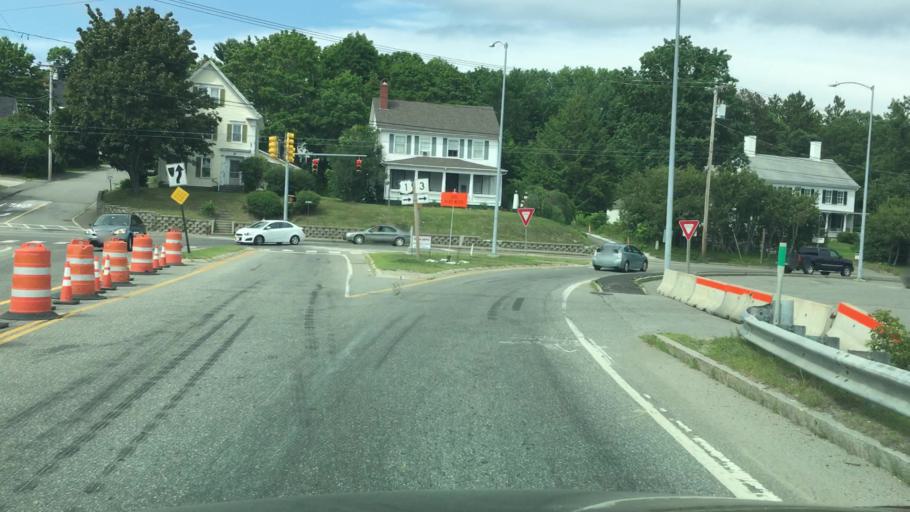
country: US
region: Maine
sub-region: Hancock County
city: Bucksport
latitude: 44.5707
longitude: -68.7876
